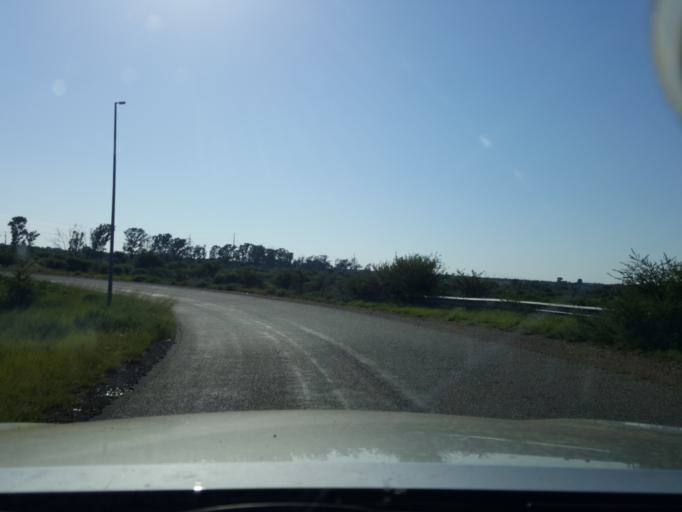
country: ZA
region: North-West
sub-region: Ngaka Modiri Molema District Municipality
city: Mahikeng
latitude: -25.8524
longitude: 25.6805
